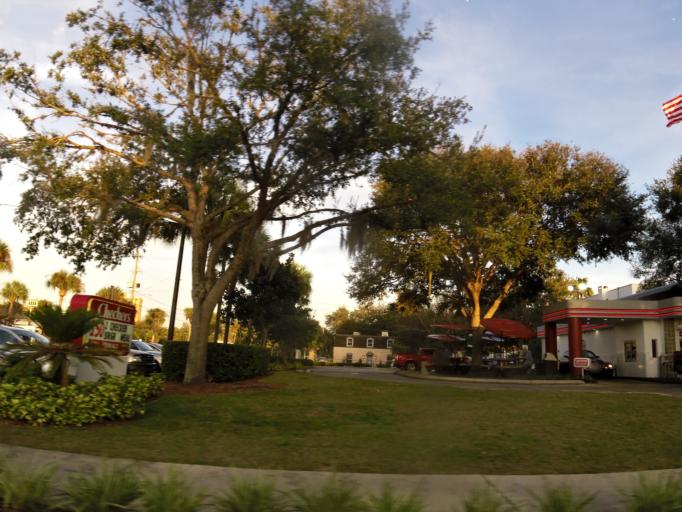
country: US
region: Florida
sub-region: Volusia County
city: DeLand
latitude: 29.0269
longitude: -81.3033
